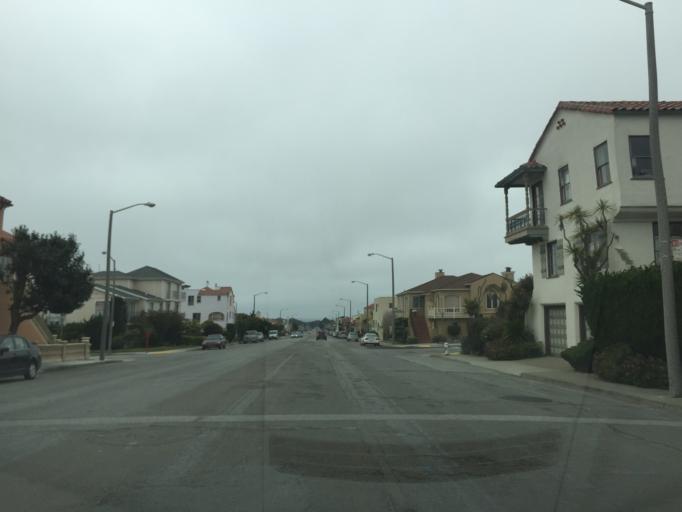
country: US
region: California
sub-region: San Mateo County
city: Daly City
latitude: 37.7326
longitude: -122.4796
